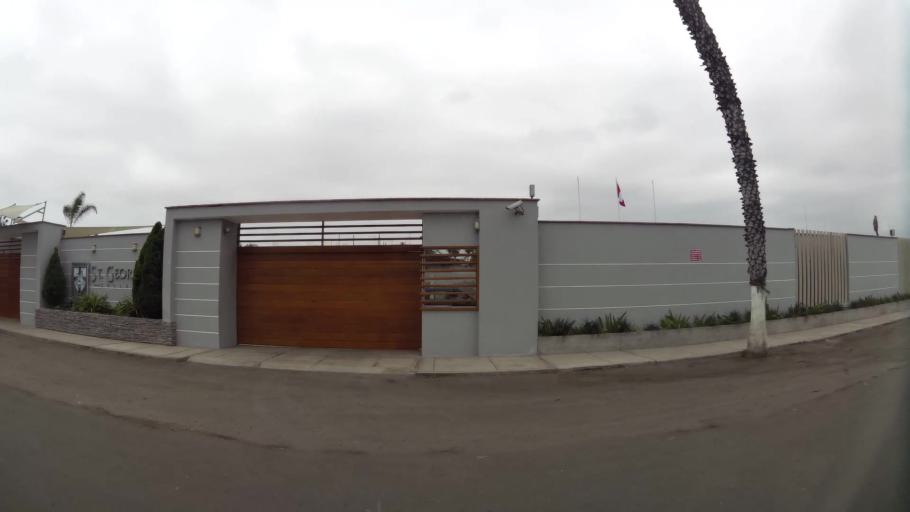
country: PE
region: Lima
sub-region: Lima
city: Surco
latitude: -12.2097
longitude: -77.0020
